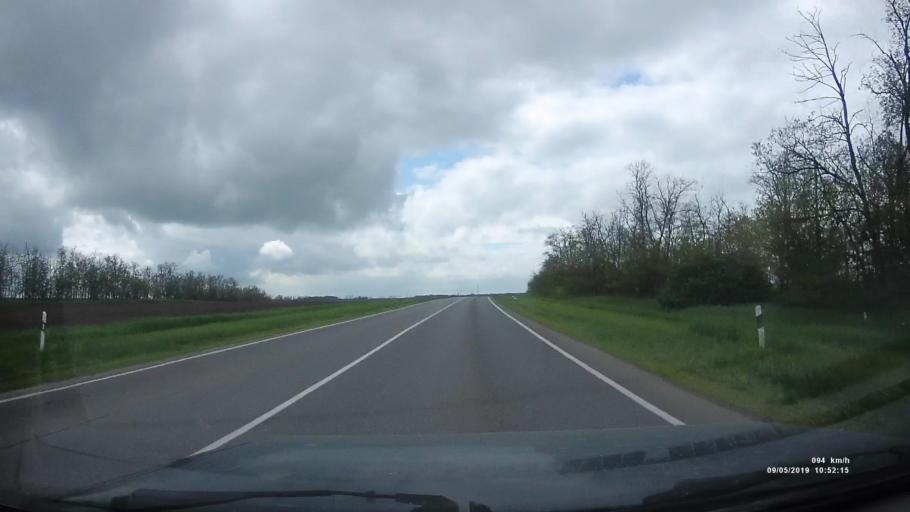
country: RU
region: Rostov
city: Peshkovo
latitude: 46.9029
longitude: 39.3534
